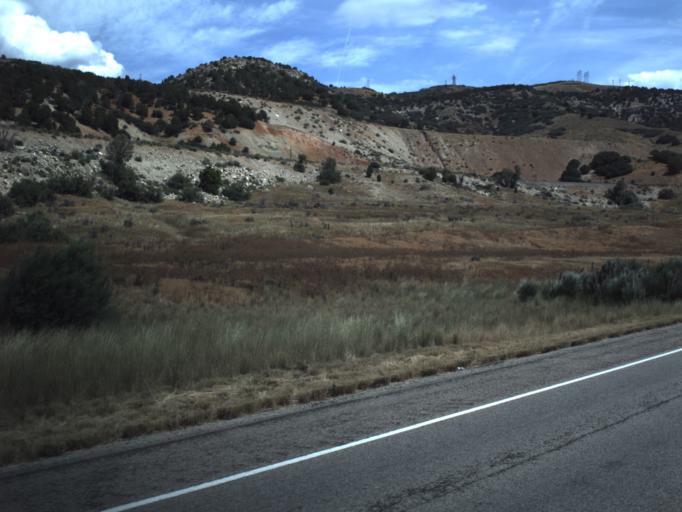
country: US
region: Utah
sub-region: Utah County
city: Woodland Hills
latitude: 39.9955
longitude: -111.4879
